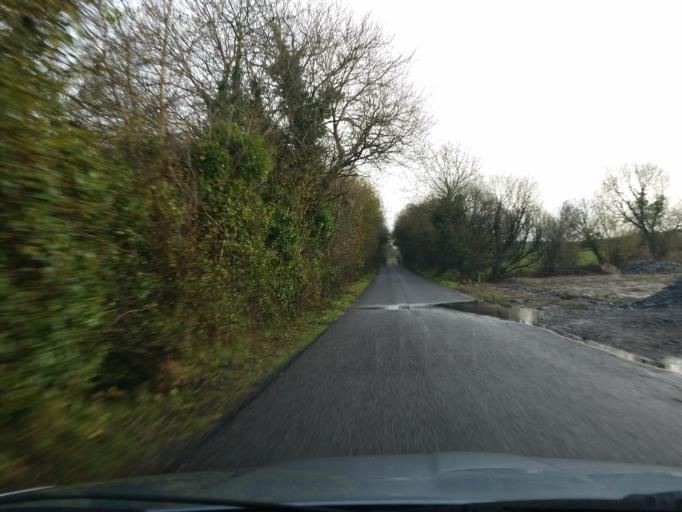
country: GB
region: Northern Ireland
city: Lisnaskea
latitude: 54.2435
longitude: -7.3785
